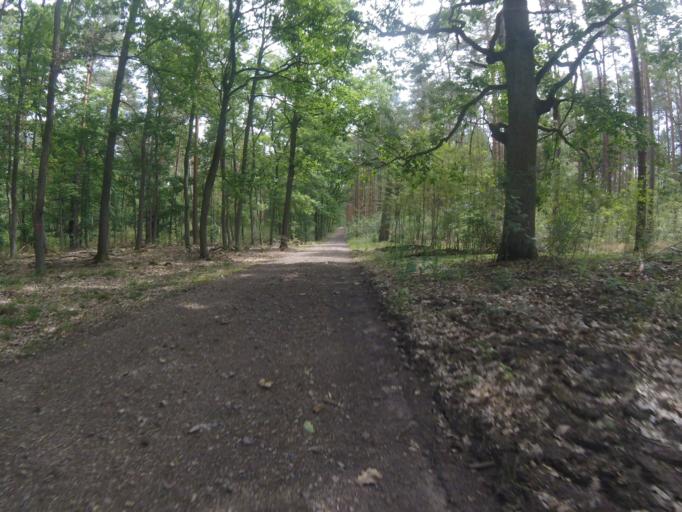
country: DE
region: Brandenburg
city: Gross Koris
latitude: 52.1975
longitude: 13.6903
